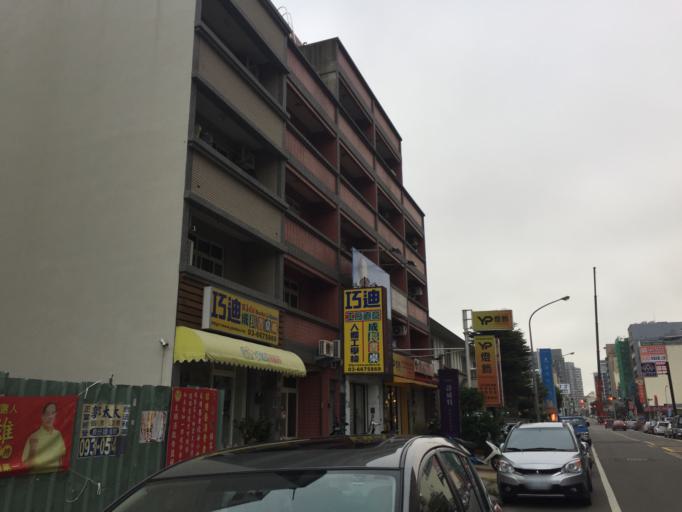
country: TW
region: Taiwan
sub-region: Hsinchu
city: Zhubei
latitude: 24.8198
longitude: 121.0224
